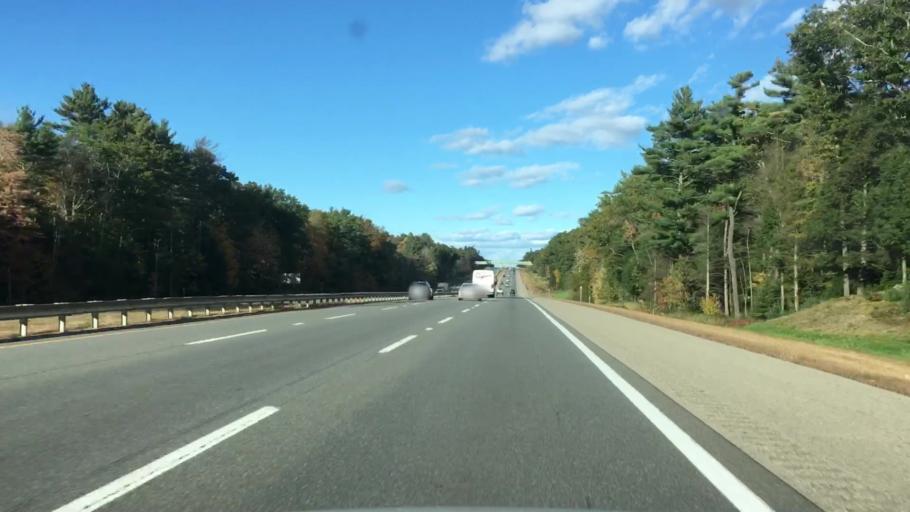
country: US
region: Maine
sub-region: York County
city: Wells Beach Station
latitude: 43.3492
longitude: -70.5935
